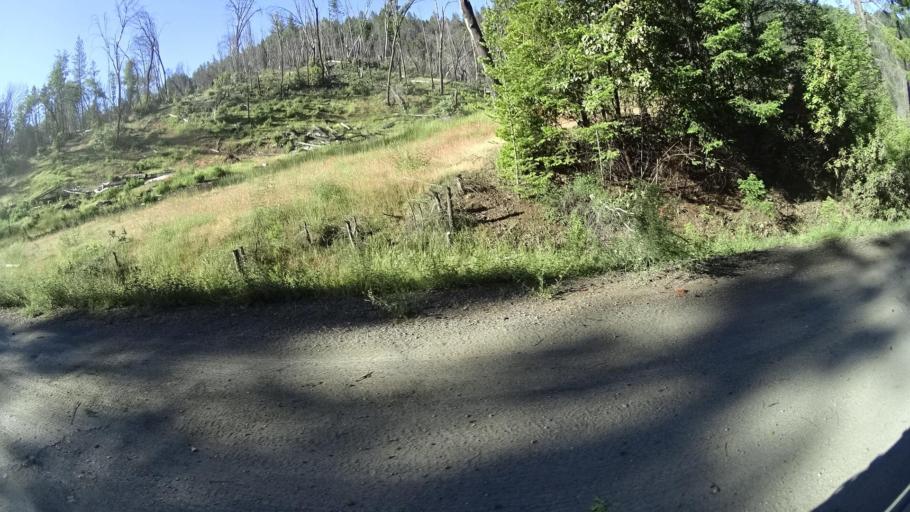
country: US
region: California
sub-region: Lake County
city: Upper Lake
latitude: 39.4034
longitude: -122.9641
